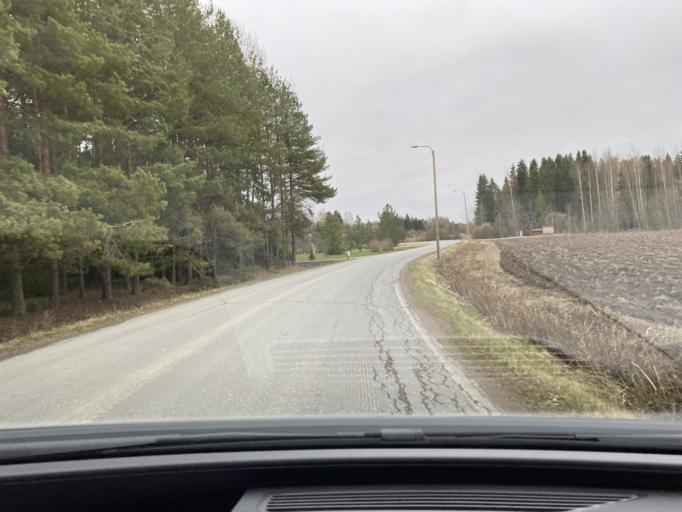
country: FI
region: Satakunta
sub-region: Pori
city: Huittinen
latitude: 61.1652
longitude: 22.7245
